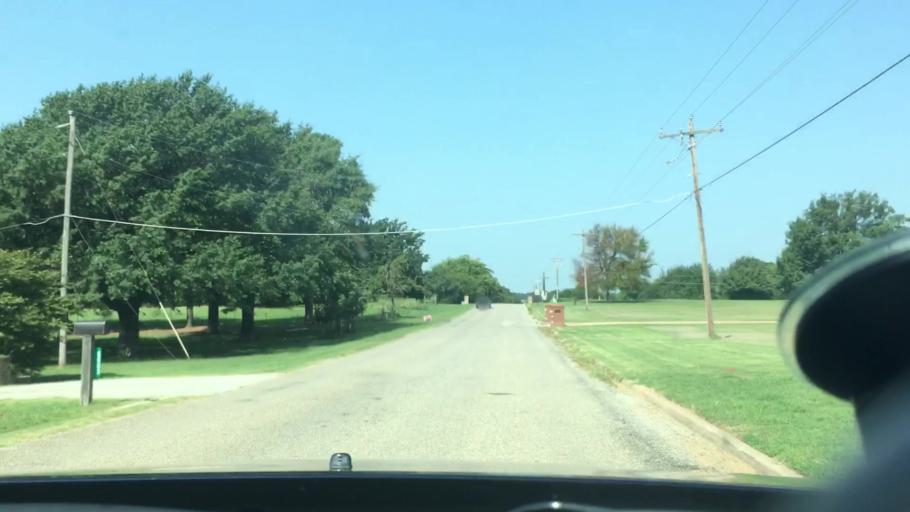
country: US
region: Oklahoma
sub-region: Bryan County
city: Durant
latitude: 34.0121
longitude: -96.4401
